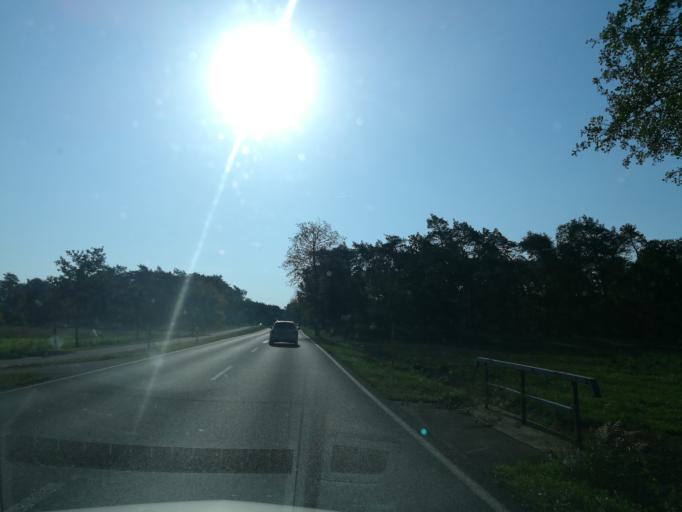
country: DE
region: Saxony-Anhalt
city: Wahlitz
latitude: 52.0958
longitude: 11.7883
